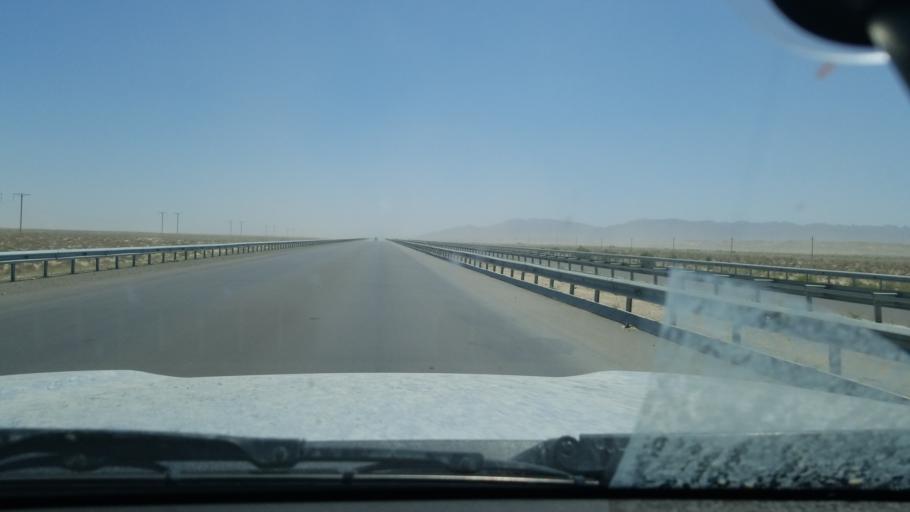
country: TM
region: Balkan
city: Gazanjyk
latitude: 39.2599
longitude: 55.3216
